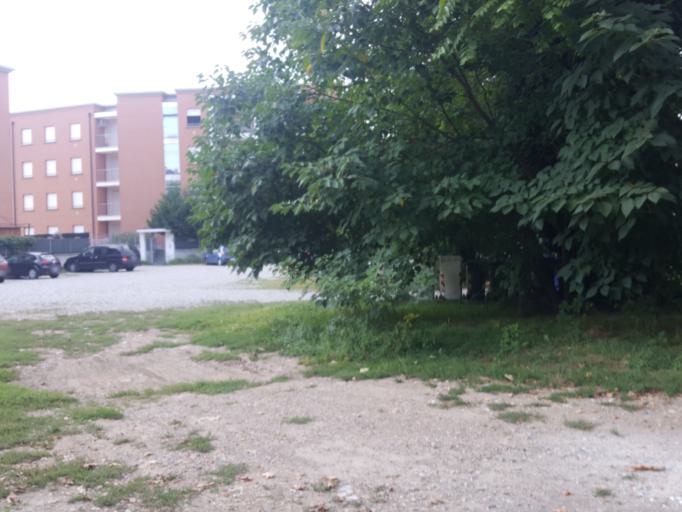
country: IT
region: Lombardy
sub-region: Citta metropolitana di Milano
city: Abbiategrasso
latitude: 45.3906
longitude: 8.9121
